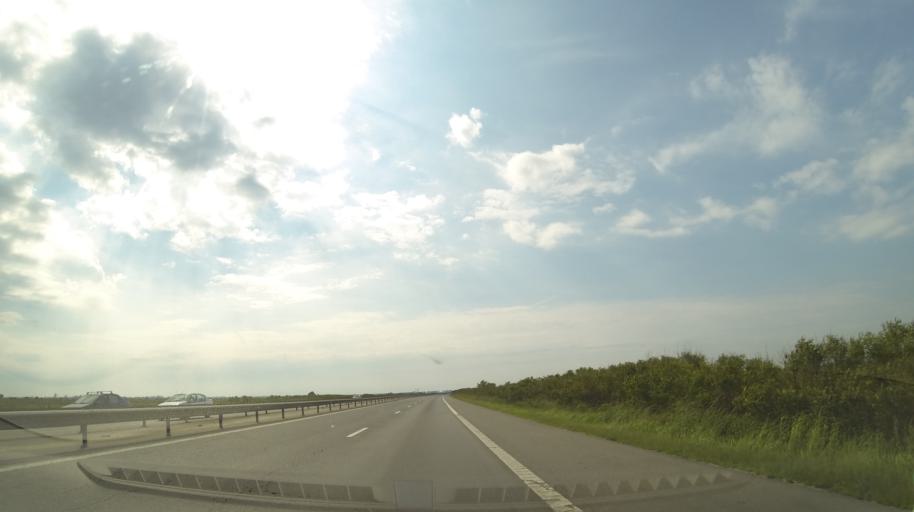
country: RO
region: Dambovita
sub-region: Comuna Corbii Mari
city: Corbii Mari
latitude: 44.5620
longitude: 25.4939
